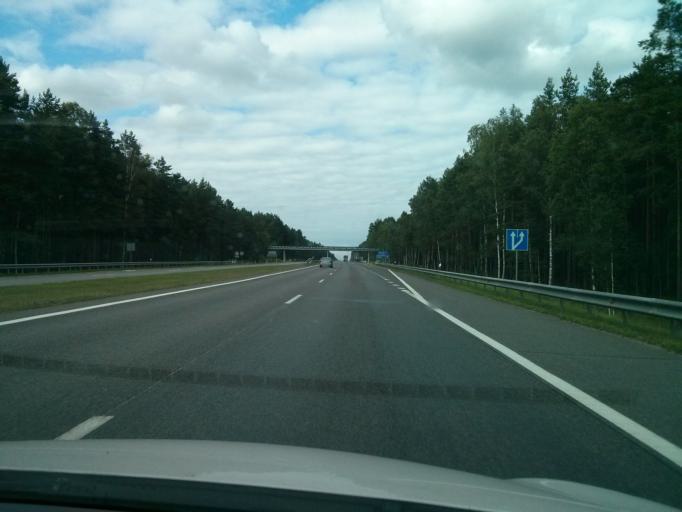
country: BY
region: Minsk
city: Zamostochcha
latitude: 53.8898
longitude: 27.9408
